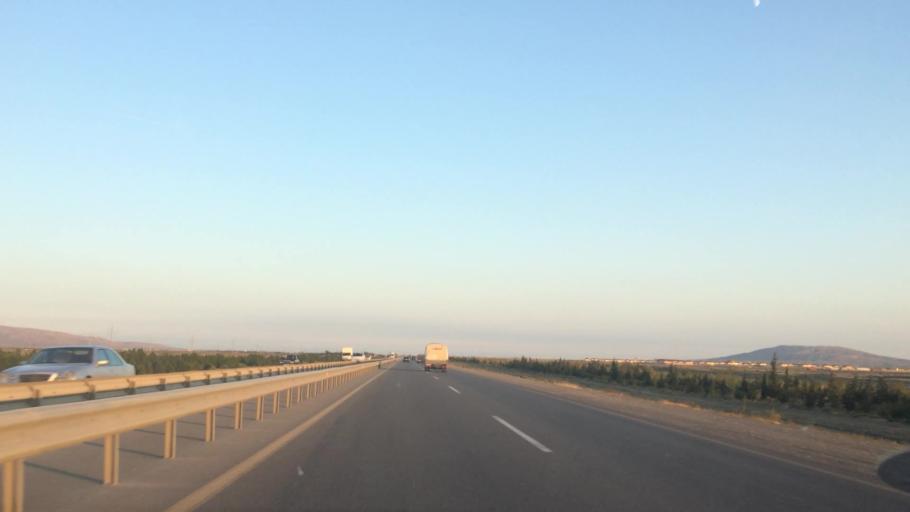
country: AZ
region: Baki
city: Qobustan
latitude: 39.9898
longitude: 49.1994
